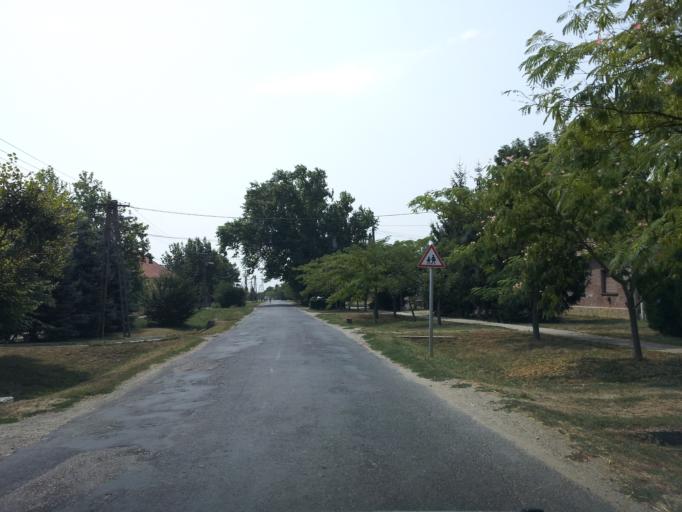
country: HU
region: Gyor-Moson-Sopron
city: Mihalyi
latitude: 47.5230
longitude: 17.1668
